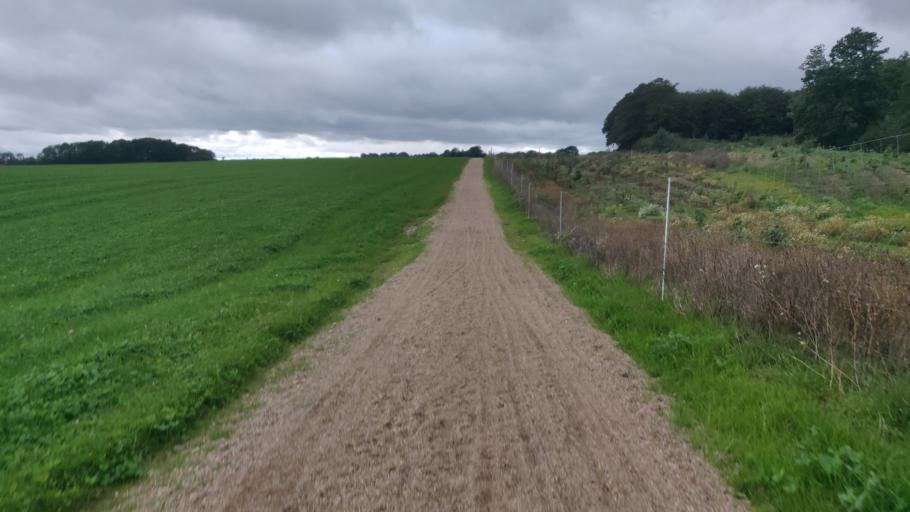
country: DK
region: South Denmark
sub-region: Kolding Kommune
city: Lunderskov
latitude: 55.5390
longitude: 9.3472
